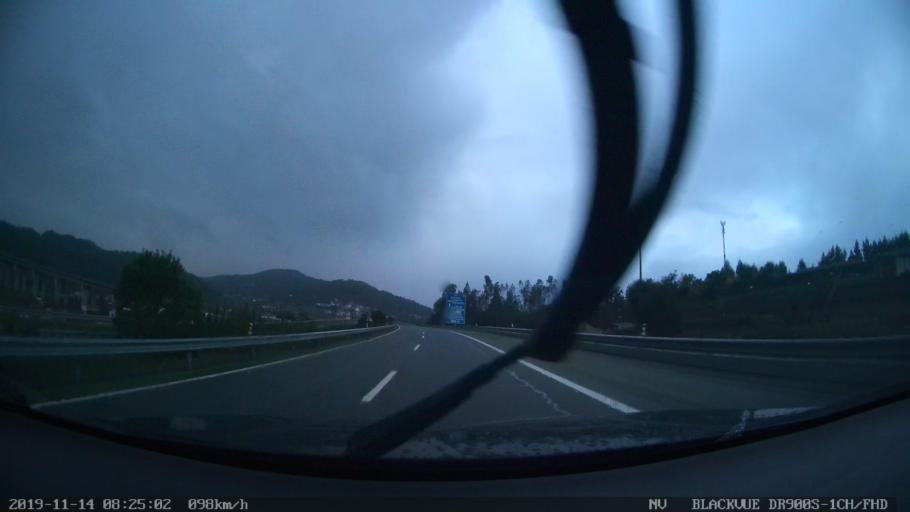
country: PT
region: Braga
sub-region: Braga
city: Oliveira
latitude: 41.5313
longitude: -8.4805
